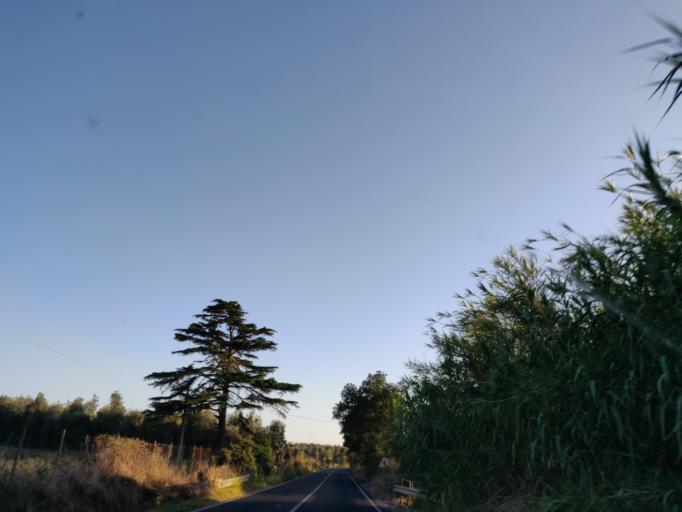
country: IT
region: Latium
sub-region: Provincia di Viterbo
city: Canino
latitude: 42.4276
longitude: 11.7118
